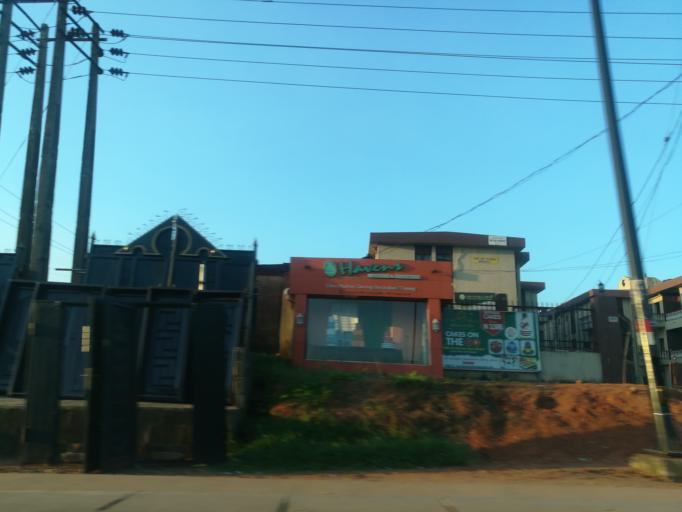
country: NG
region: Lagos
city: Ikorodu
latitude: 6.6250
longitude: 3.4915
